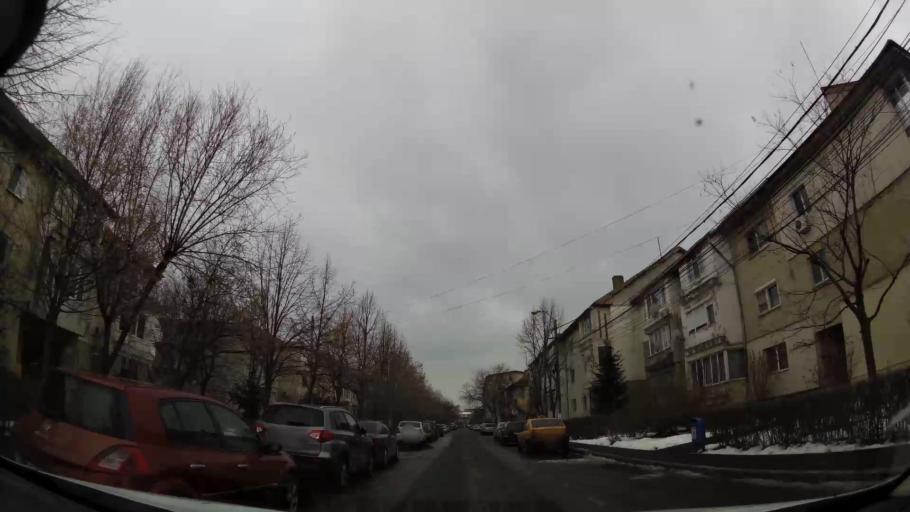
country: RO
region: Ilfov
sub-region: Comuna Otopeni
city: Otopeni
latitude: 44.5492
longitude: 26.0704
